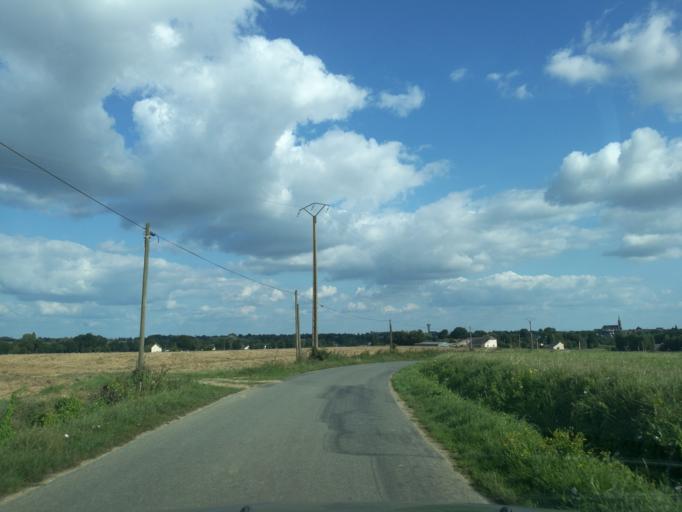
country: FR
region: Brittany
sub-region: Departement d'Ille-et-Vilaine
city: Bedee
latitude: 48.1921
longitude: -1.9603
